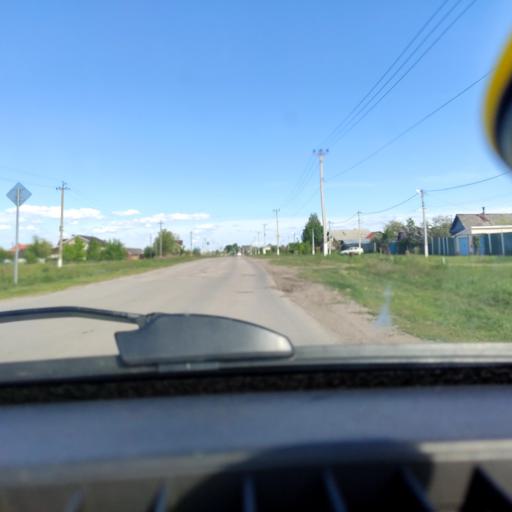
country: RU
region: Samara
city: Podstepki
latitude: 53.5193
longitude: 49.1219
